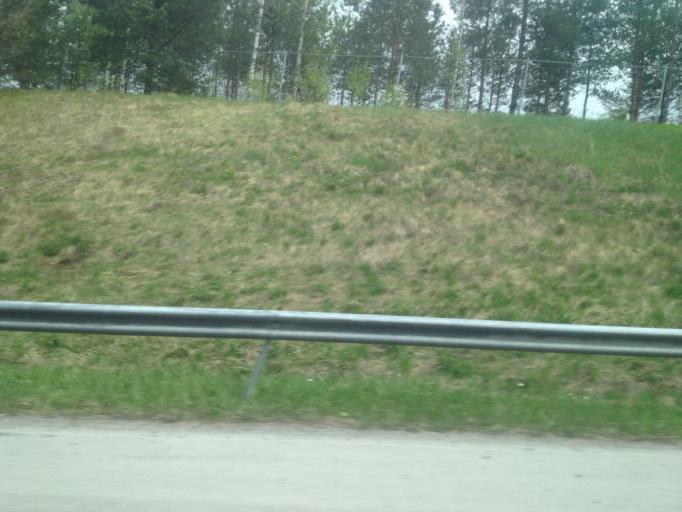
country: FI
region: Uusimaa
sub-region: Helsinki
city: Hyvinge
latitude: 60.5885
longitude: 24.7983
